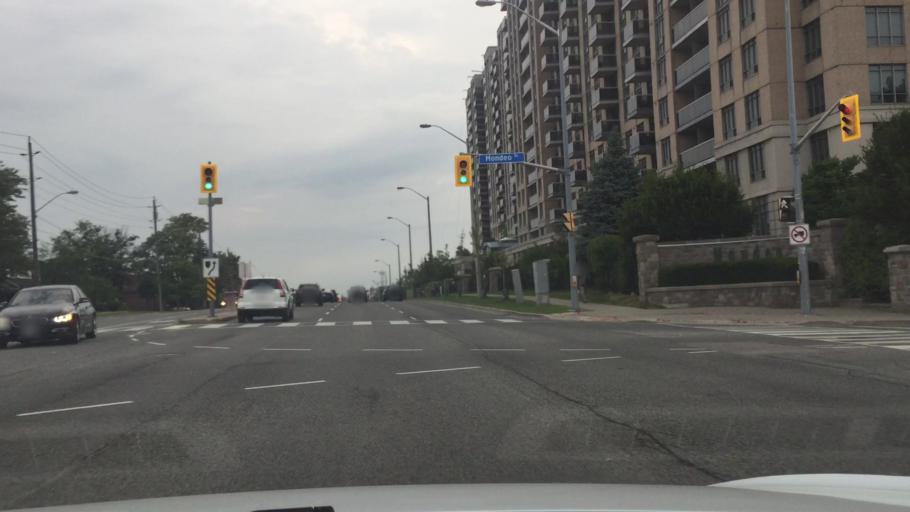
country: CA
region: Ontario
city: Scarborough
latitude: 43.7644
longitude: -79.2877
